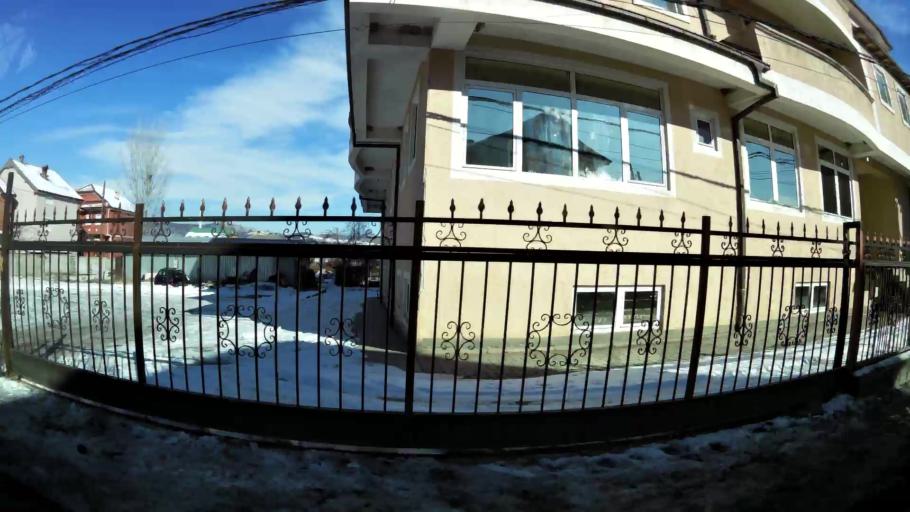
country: MK
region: Saraj
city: Saraj
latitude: 42.0008
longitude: 21.3208
